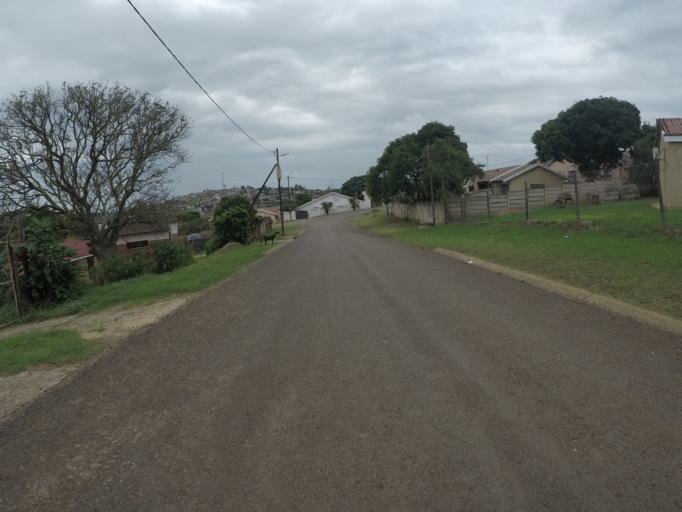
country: ZA
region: KwaZulu-Natal
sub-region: uThungulu District Municipality
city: Empangeni
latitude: -28.7778
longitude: 31.8618
